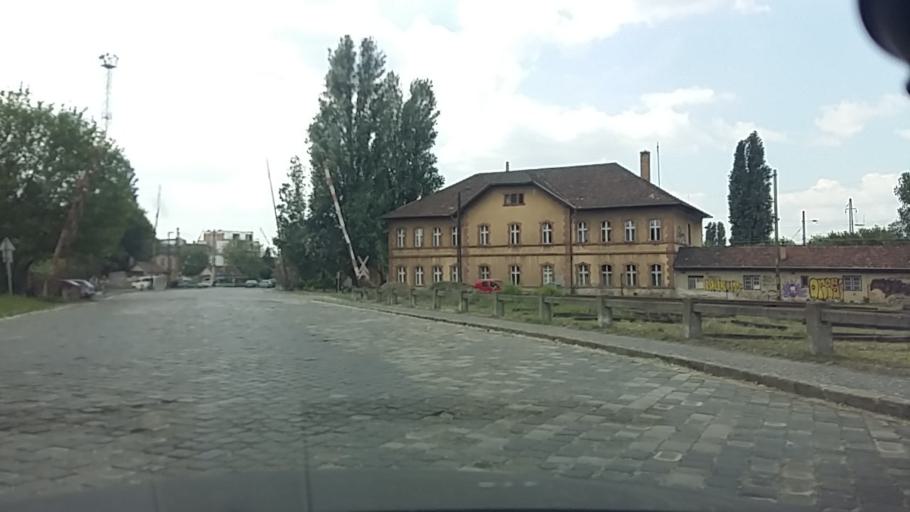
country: HU
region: Budapest
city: Budapest XIII. keruelet
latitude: 47.5251
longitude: 19.0911
